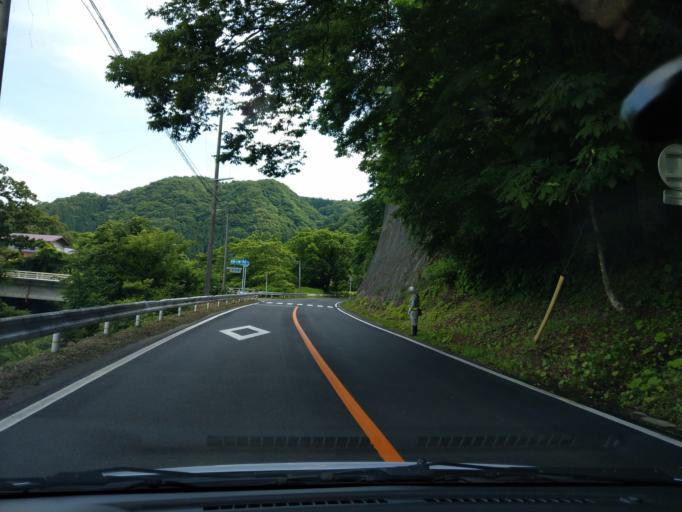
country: JP
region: Akita
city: Kakunodatemachi
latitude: 39.7480
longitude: 140.5998
